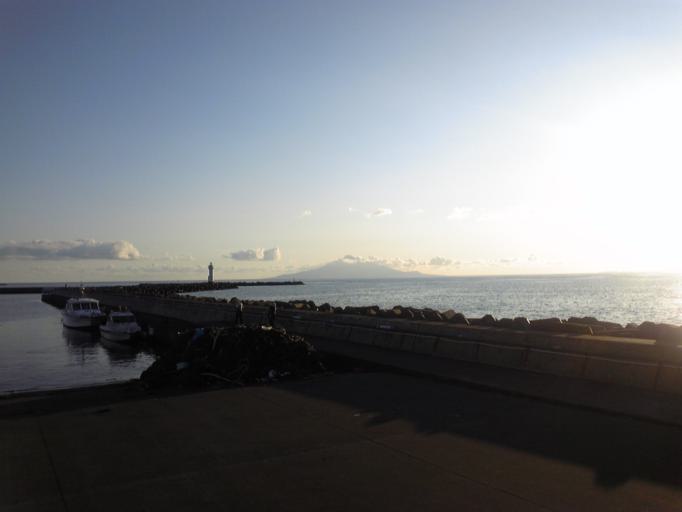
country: JP
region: Hokkaido
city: Wakkanai
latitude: 45.4485
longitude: 141.6435
